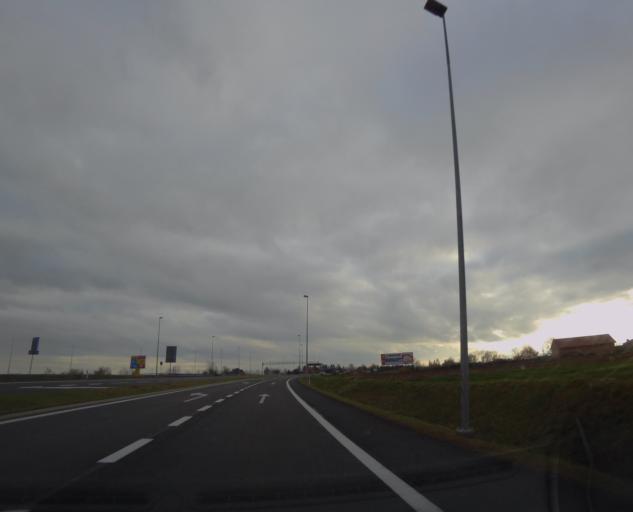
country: PL
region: Subcarpathian Voivodeship
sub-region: Powiat jaroslawski
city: Radymno
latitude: 49.9325
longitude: 22.8201
